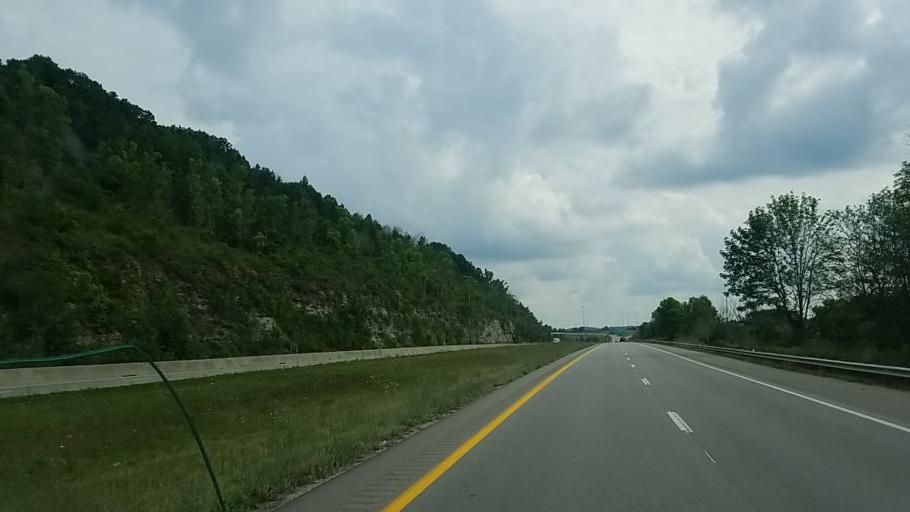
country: US
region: Ohio
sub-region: Guernsey County
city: Cambridge
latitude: 40.0102
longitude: -81.5597
